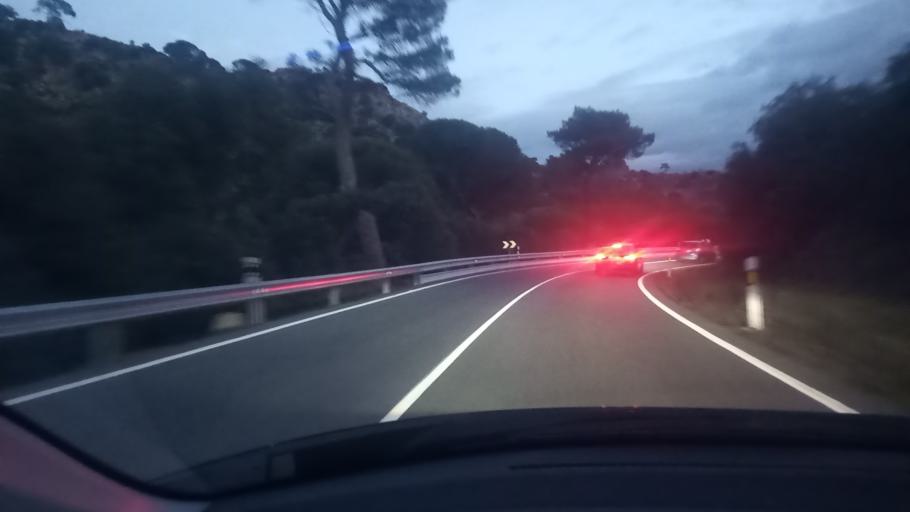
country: ES
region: Madrid
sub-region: Provincia de Madrid
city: Navas del Rey
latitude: 40.4391
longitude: -4.2650
